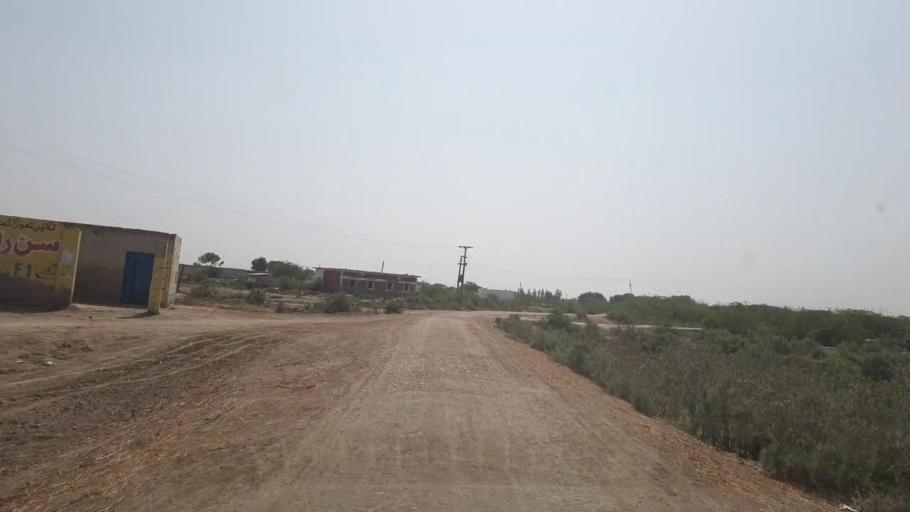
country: PK
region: Sindh
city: Jati
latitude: 24.4691
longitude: 68.5566
